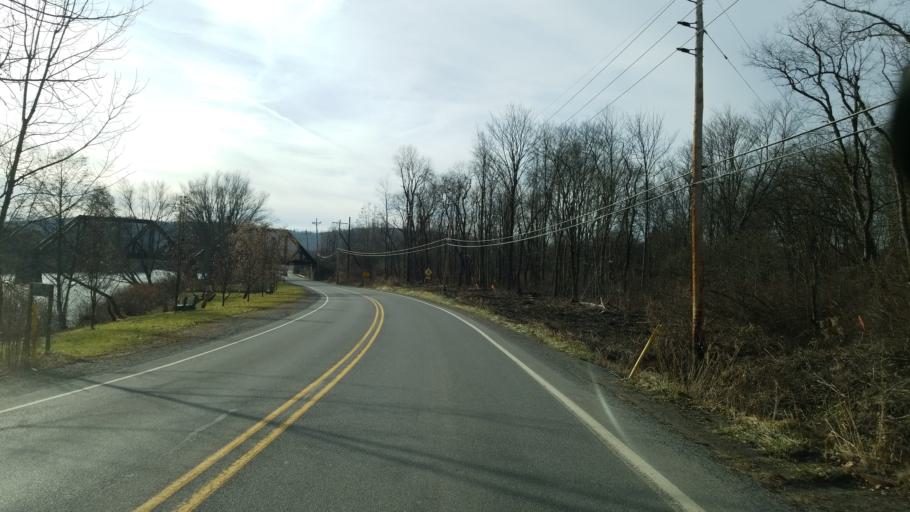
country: US
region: Pennsylvania
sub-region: Clearfield County
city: Clearfield
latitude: 41.0338
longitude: -78.4320
